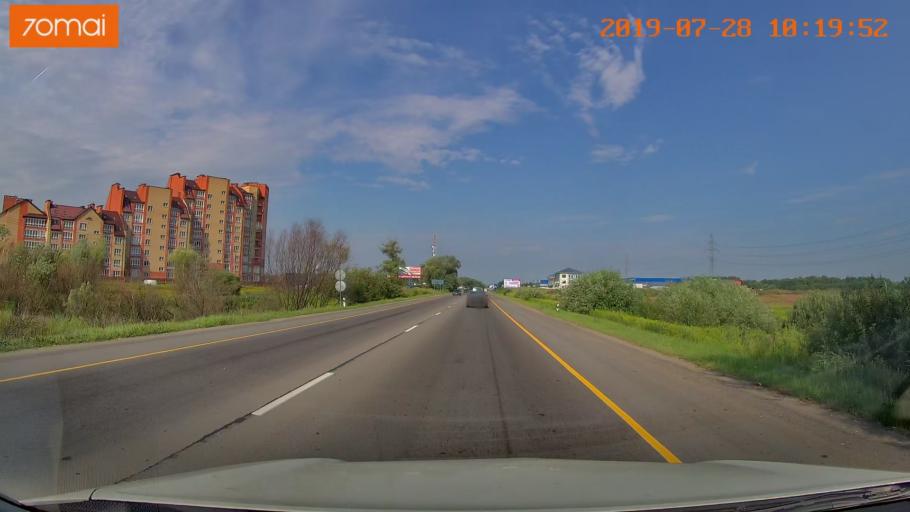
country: RU
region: Kaliningrad
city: Maloye Isakovo
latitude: 54.7485
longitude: 20.5823
